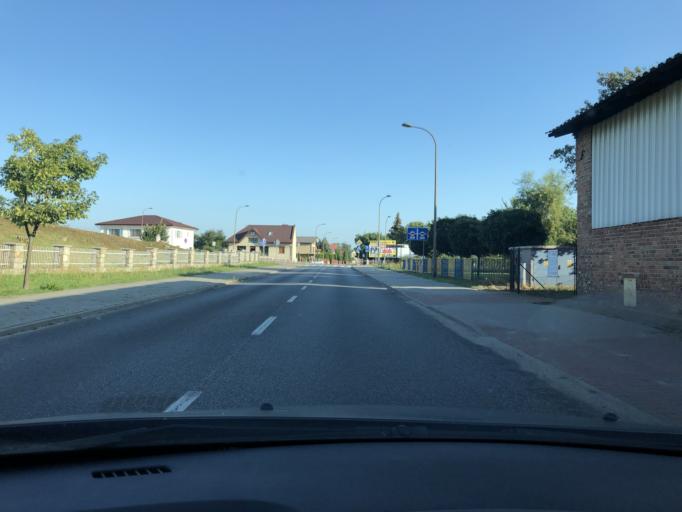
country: PL
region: Lodz Voivodeship
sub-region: Powiat wieruszowski
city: Wieruszow
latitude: 51.2906
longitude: 18.1615
